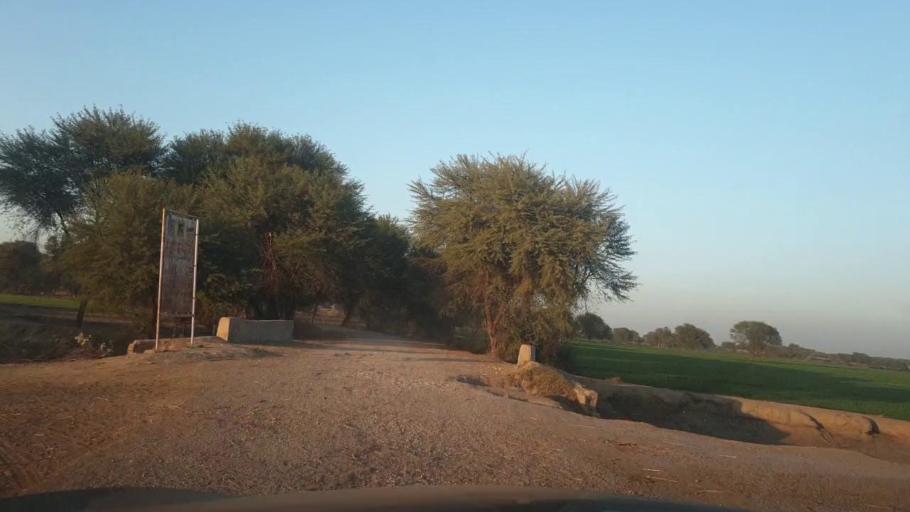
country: PK
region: Sindh
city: Ubauro
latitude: 28.1850
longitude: 69.6023
